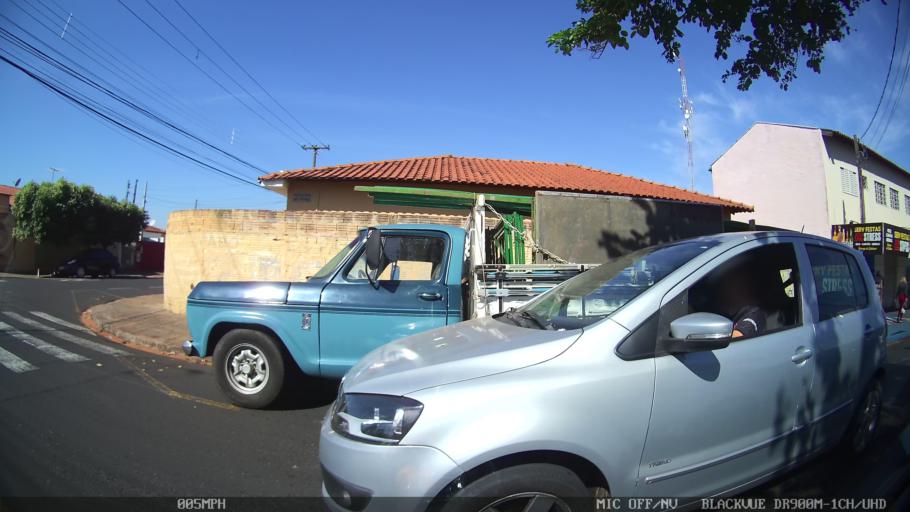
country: BR
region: Sao Paulo
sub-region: Sao Jose Do Rio Preto
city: Sao Jose do Rio Preto
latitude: -20.7802
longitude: -49.4081
